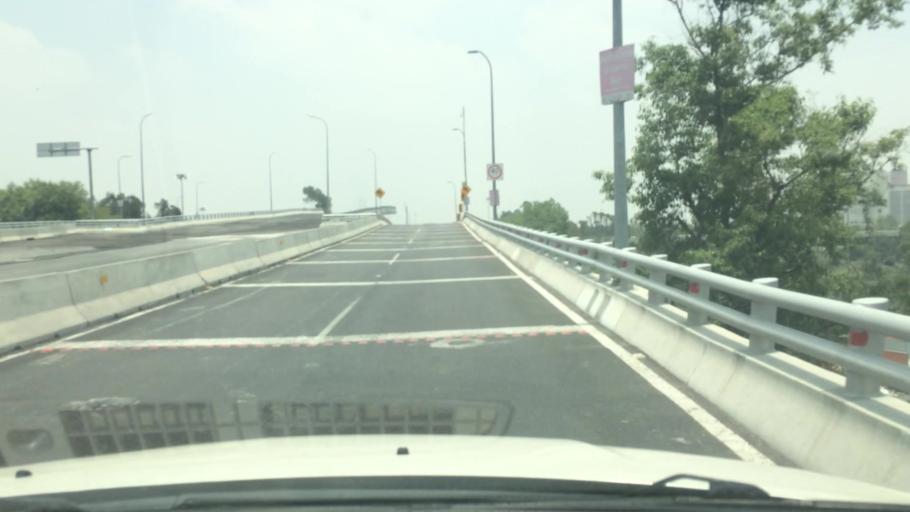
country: MX
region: Mexico City
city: Tlalpan
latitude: 19.2887
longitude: -99.1534
